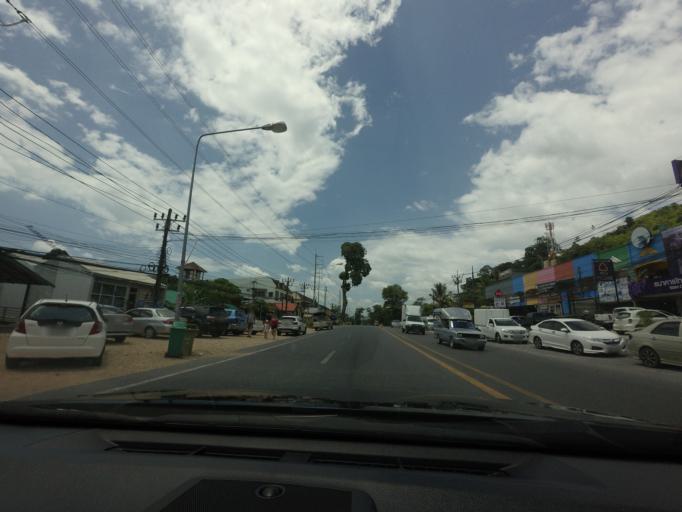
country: TH
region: Phangnga
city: Ban Khao Lak
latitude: 8.6483
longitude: 98.2524
